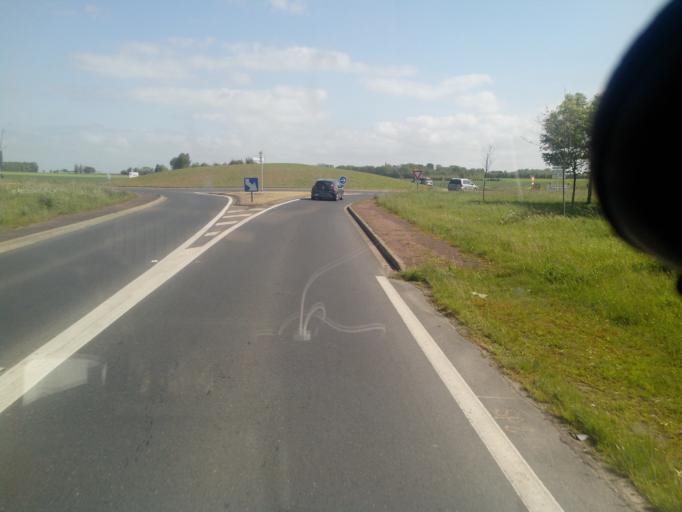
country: FR
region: Lower Normandy
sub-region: Departement du Calvados
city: Bernieres-sur-Mer
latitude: 49.3043
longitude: -0.4376
